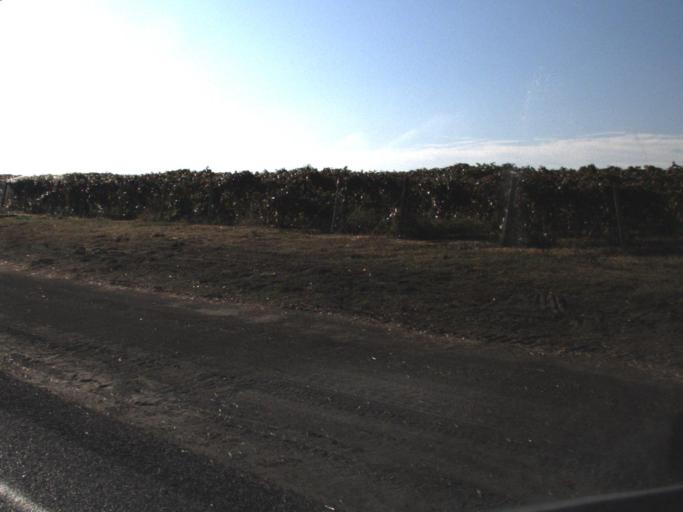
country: US
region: Washington
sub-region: Walla Walla County
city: Burbank
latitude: 46.2386
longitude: -118.8324
